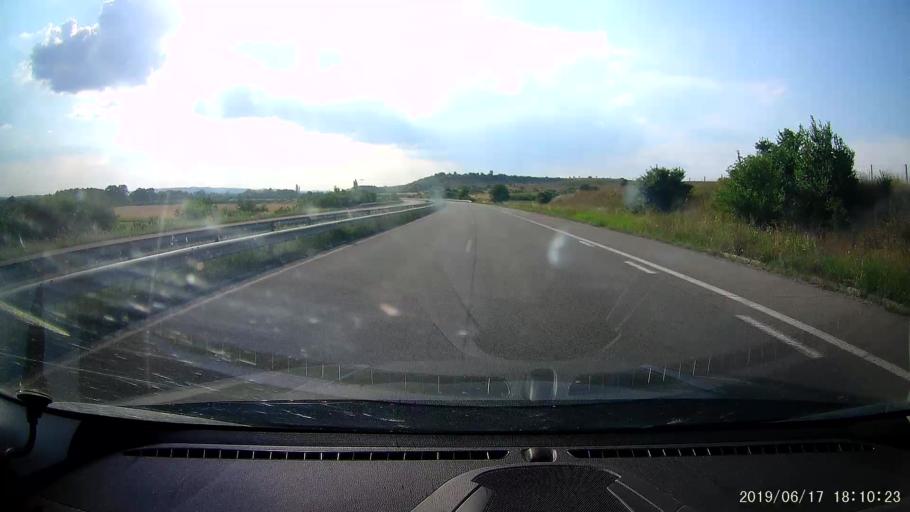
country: BG
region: Khaskovo
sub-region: Obshtina Lyubimets
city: Lyubimets
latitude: 41.8740
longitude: 26.0785
